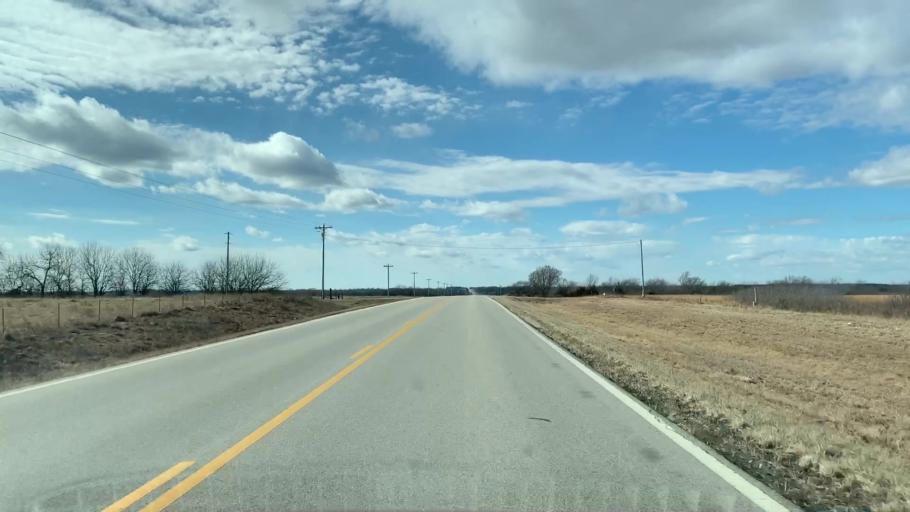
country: US
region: Kansas
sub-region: Neosho County
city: Erie
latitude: 37.5291
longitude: -95.3822
